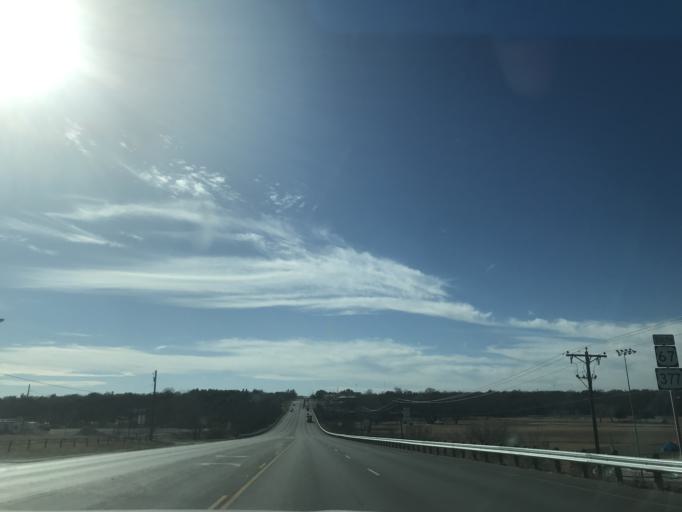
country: US
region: Texas
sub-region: Erath County
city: Stephenville
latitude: 32.2112
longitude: -98.1977
